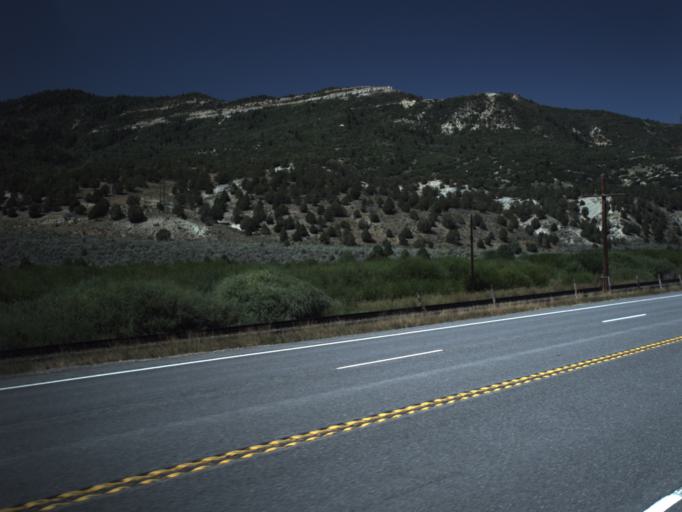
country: US
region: Utah
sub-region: Utah County
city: Mapleton
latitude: 39.9763
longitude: -111.3447
